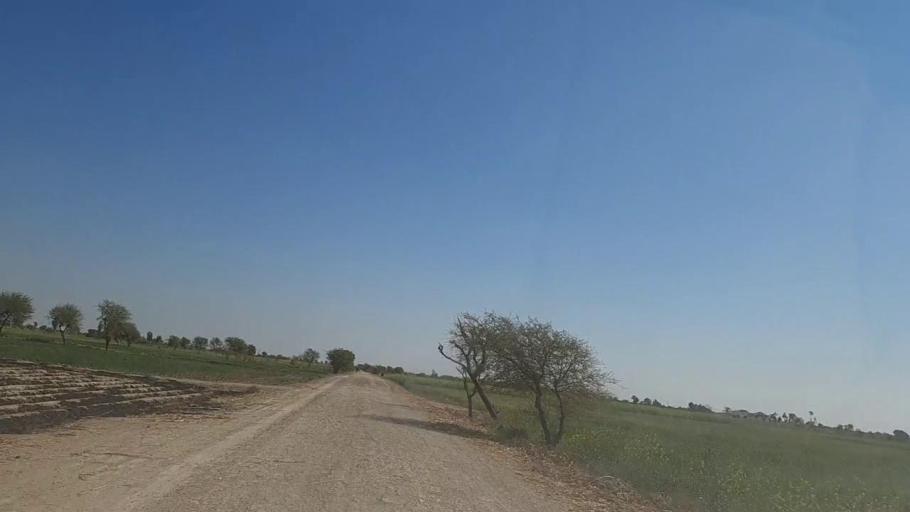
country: PK
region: Sindh
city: Digri
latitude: 25.1068
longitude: 69.1222
